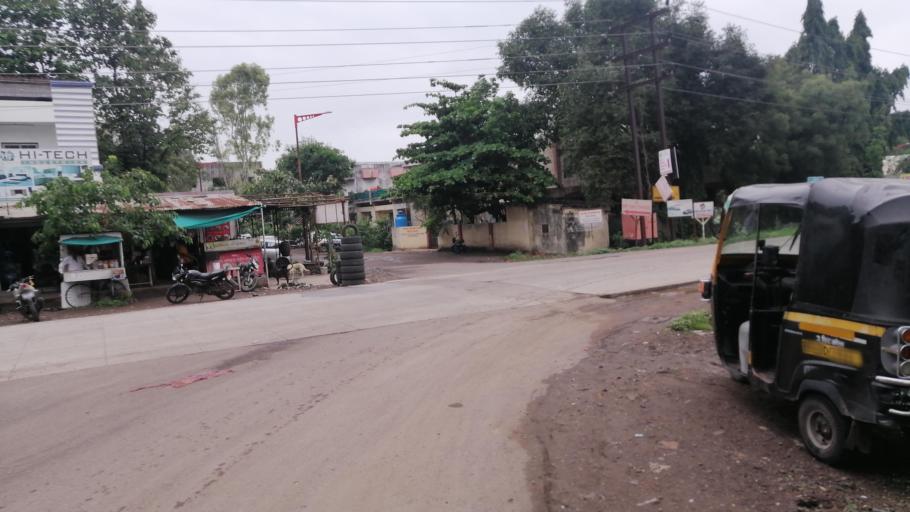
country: IN
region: Maharashtra
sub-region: Aurangabad Division
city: Aurangabad
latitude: 19.8789
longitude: 75.3773
